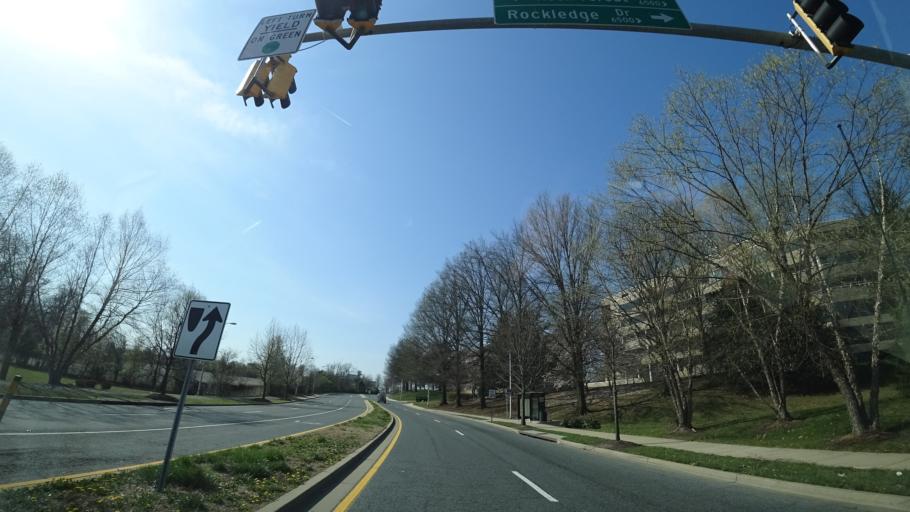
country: US
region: Maryland
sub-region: Montgomery County
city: North Bethesda
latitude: 39.0296
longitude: -77.1324
